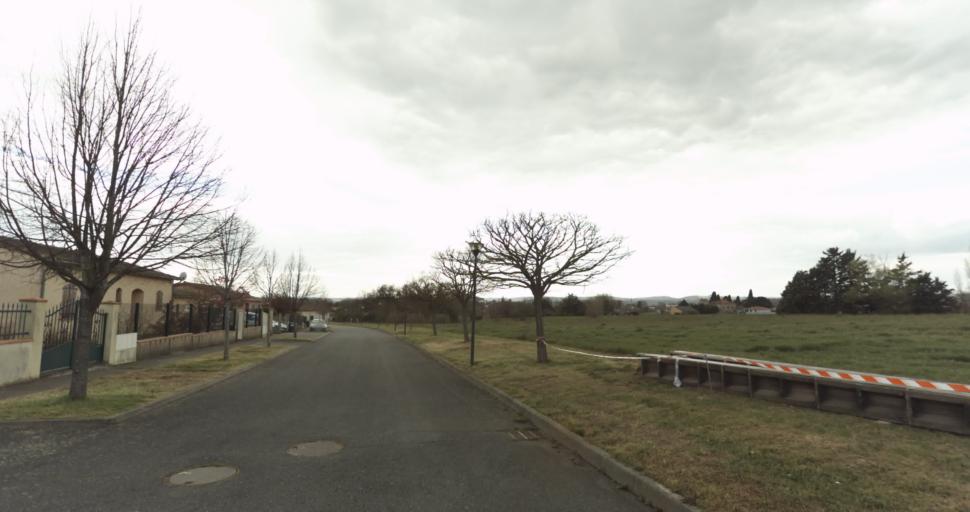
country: FR
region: Midi-Pyrenees
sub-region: Departement de la Haute-Garonne
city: Auterive
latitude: 43.3561
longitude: 1.4827
